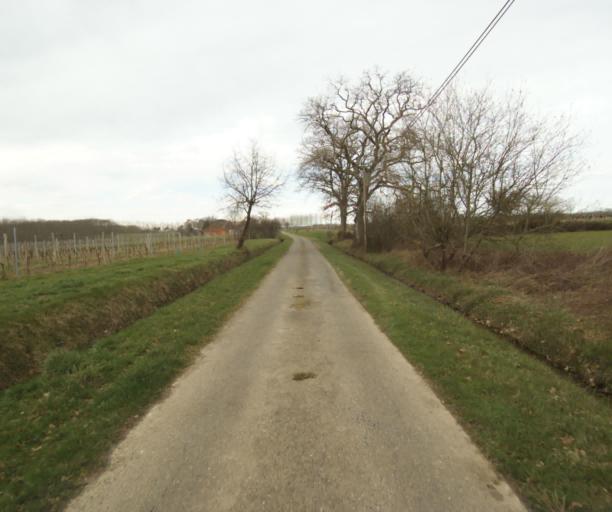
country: FR
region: Midi-Pyrenees
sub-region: Departement du Gers
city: Eauze
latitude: 43.9150
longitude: 0.0438
